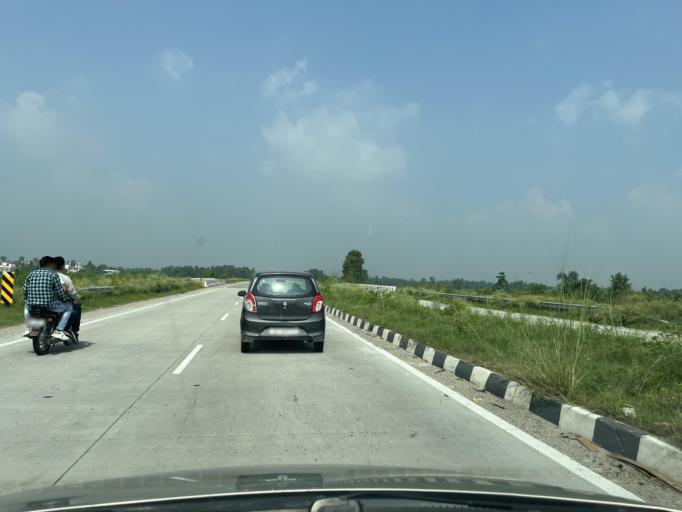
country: IN
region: Uttarakhand
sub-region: Udham Singh Nagar
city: Kashipur
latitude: 29.1642
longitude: 78.9923
